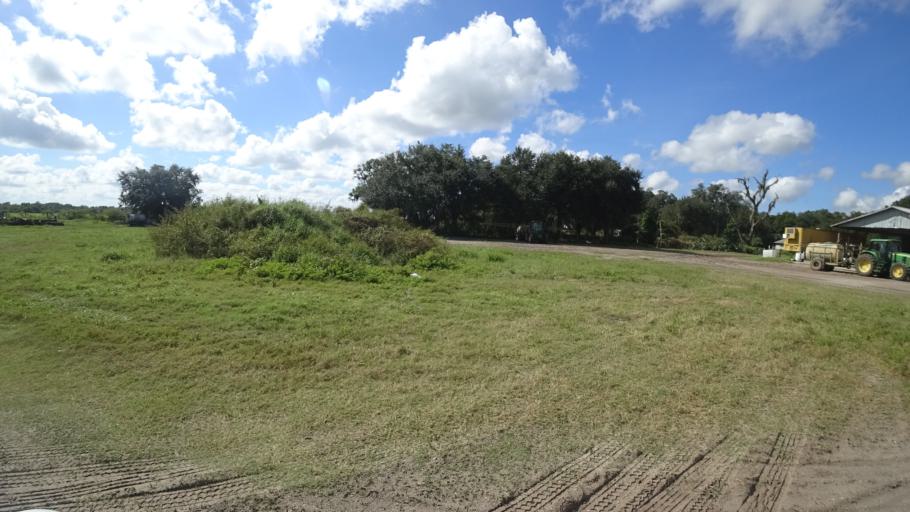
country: US
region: Florida
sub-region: DeSoto County
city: Arcadia
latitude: 27.3684
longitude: -82.1327
